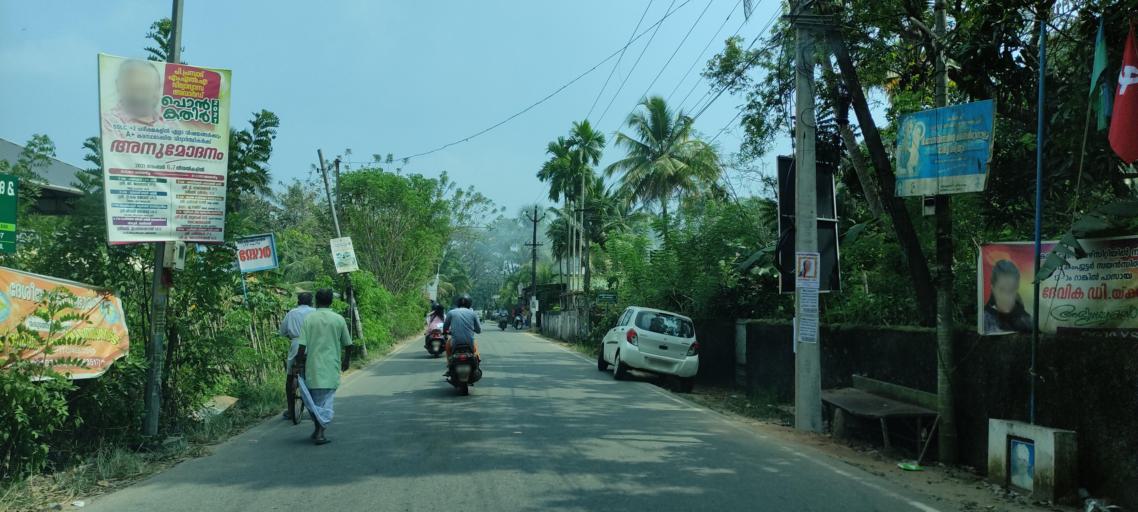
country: IN
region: Kerala
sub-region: Alappuzha
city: Shertallai
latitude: 9.6554
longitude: 76.3516
